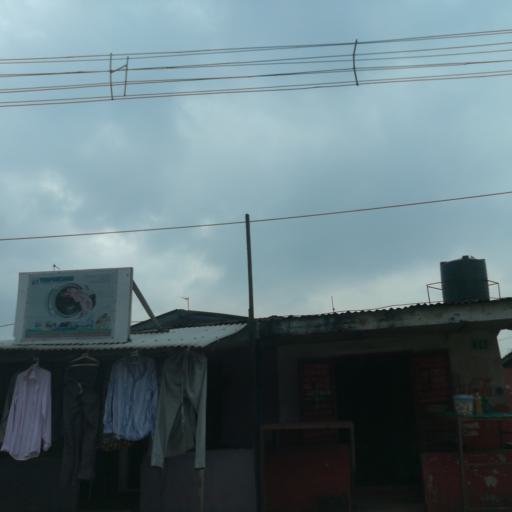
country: NG
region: Rivers
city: Port Harcourt
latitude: 4.8252
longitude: 7.0396
